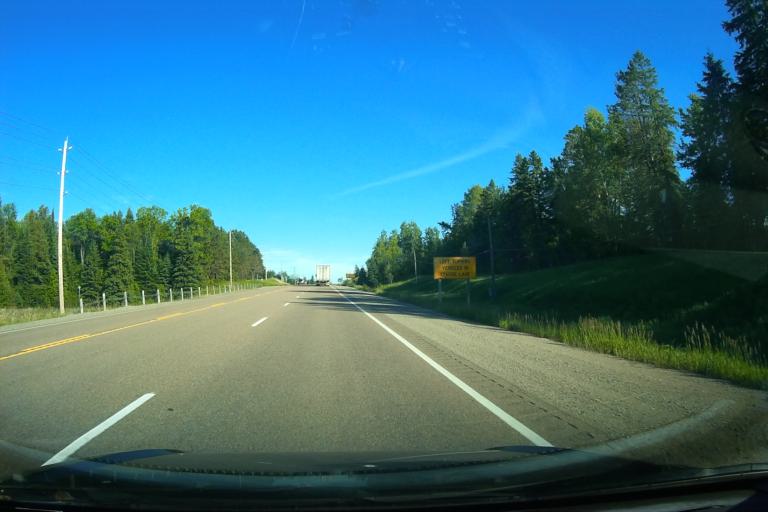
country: CA
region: Ontario
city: Renfrew
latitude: 45.6094
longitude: -76.8566
